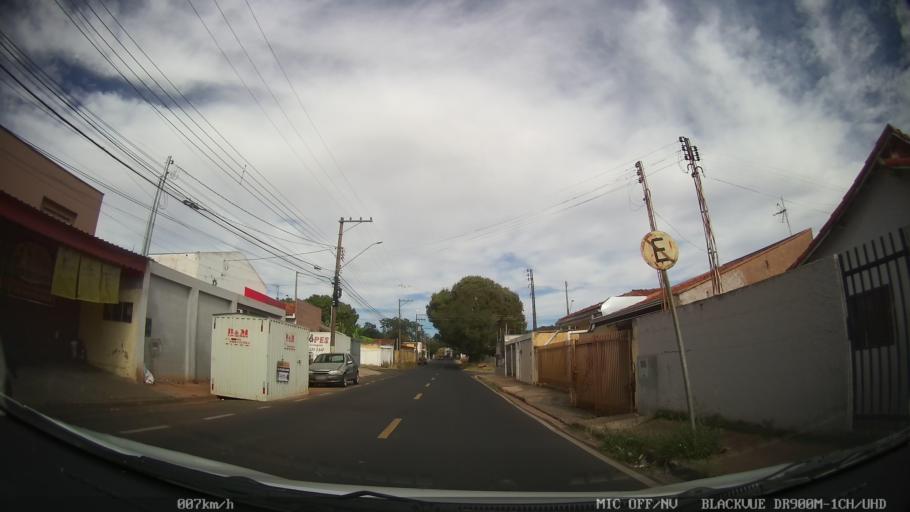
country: BR
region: Sao Paulo
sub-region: Catanduva
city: Catanduva
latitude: -21.1498
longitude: -48.9627
